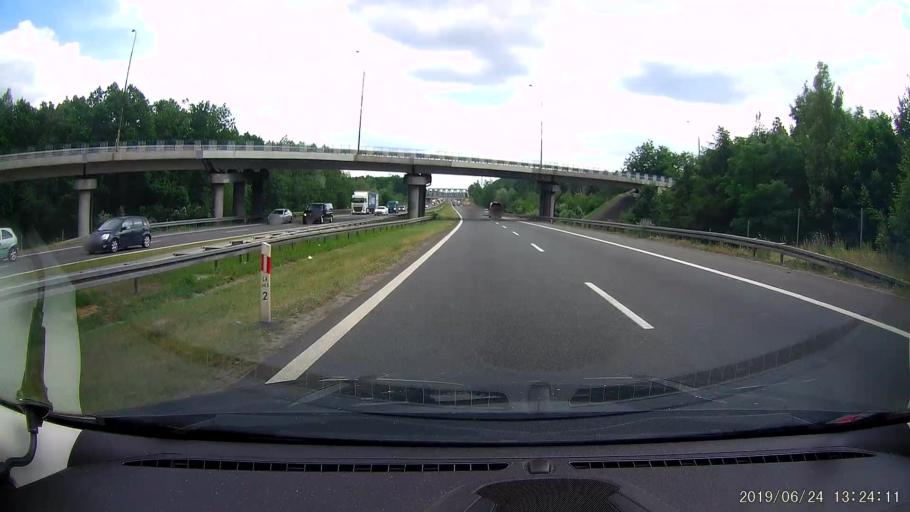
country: PL
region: Silesian Voivodeship
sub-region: Katowice
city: Murcki
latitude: 50.2308
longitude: 19.0676
